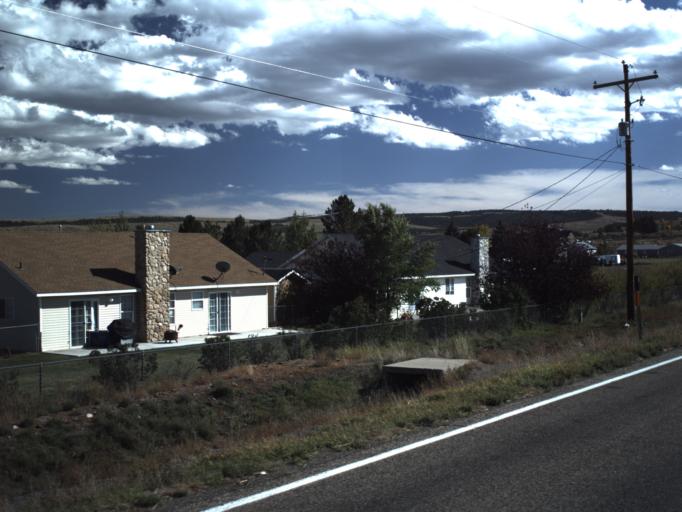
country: US
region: Utah
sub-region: Garfield County
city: Panguitch
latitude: 37.8132
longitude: -112.4355
